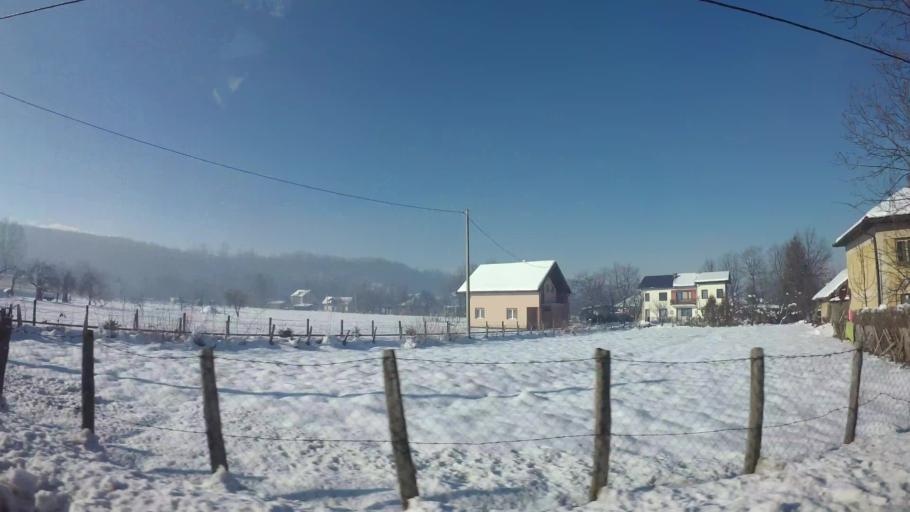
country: BA
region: Federation of Bosnia and Herzegovina
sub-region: Kanton Sarajevo
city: Sarajevo
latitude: 43.8190
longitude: 18.3820
